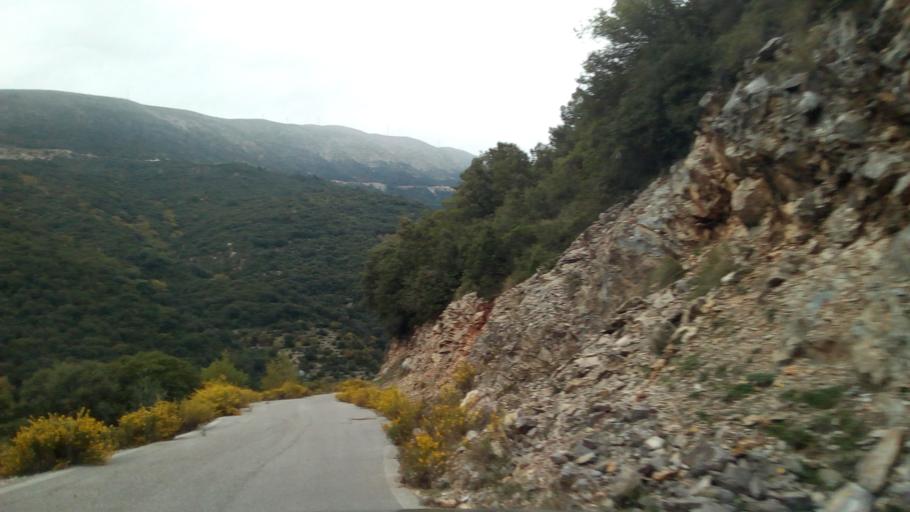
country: GR
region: West Greece
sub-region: Nomos Aitolias kai Akarnanias
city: Thermo
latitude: 38.6024
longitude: 21.8433
